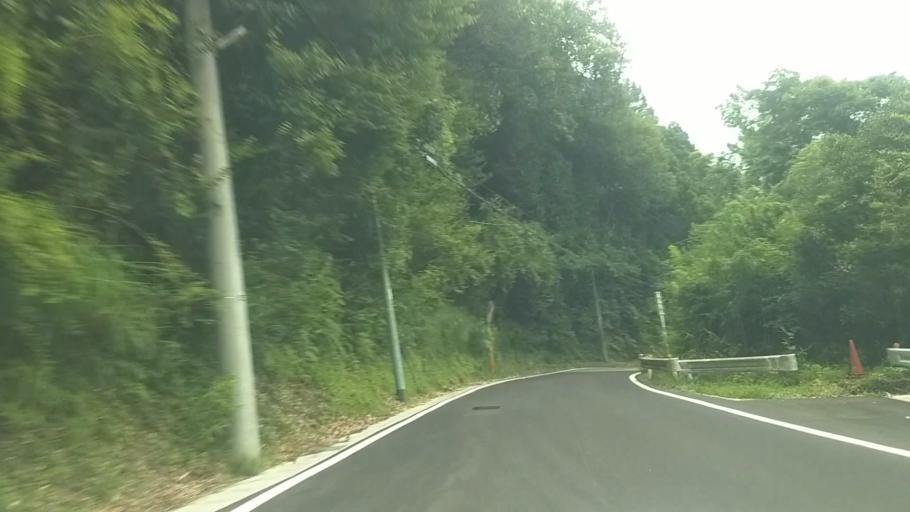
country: JP
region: Chiba
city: Kawaguchi
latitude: 35.2278
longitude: 140.0167
